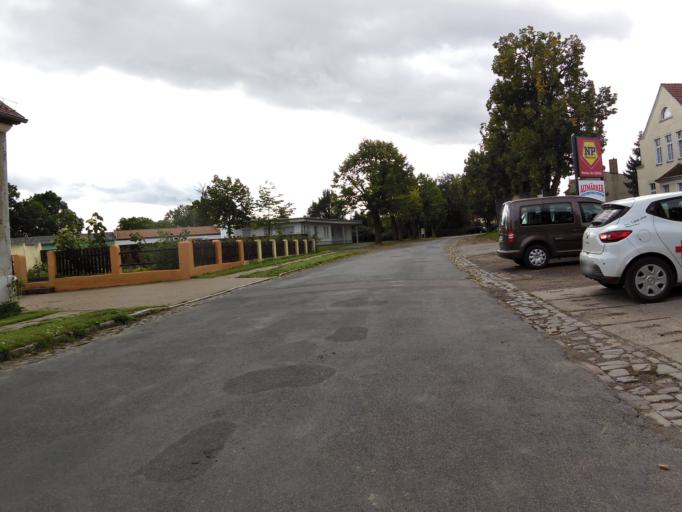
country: DE
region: Saxony-Anhalt
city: Arneburg
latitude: 52.6772
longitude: 12.0032
